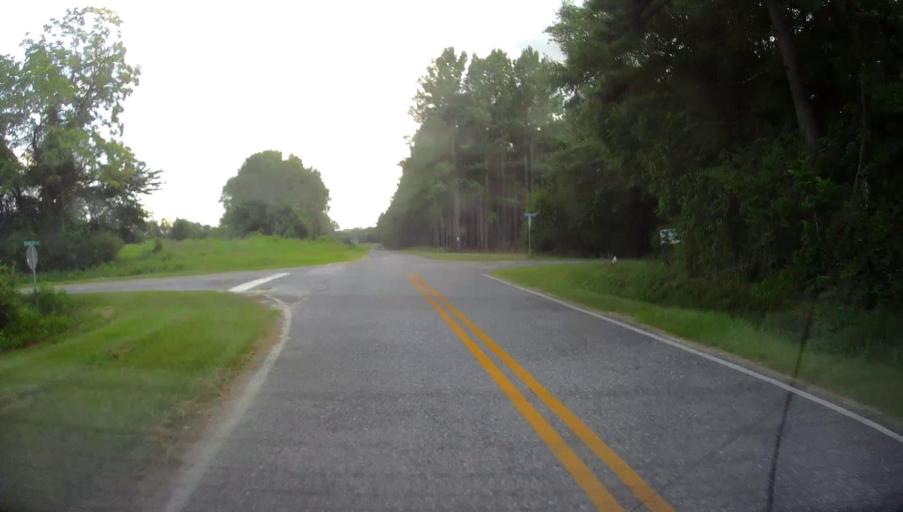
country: US
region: Georgia
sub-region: Crawford County
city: Roberta
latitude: 32.7025
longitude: -84.0164
